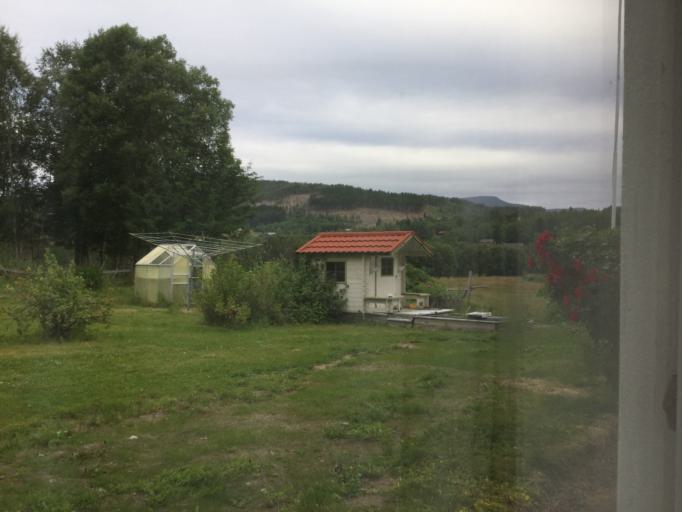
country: NO
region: More og Romsdal
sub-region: Molde
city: Hjelset
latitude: 62.7516
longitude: 7.5331
